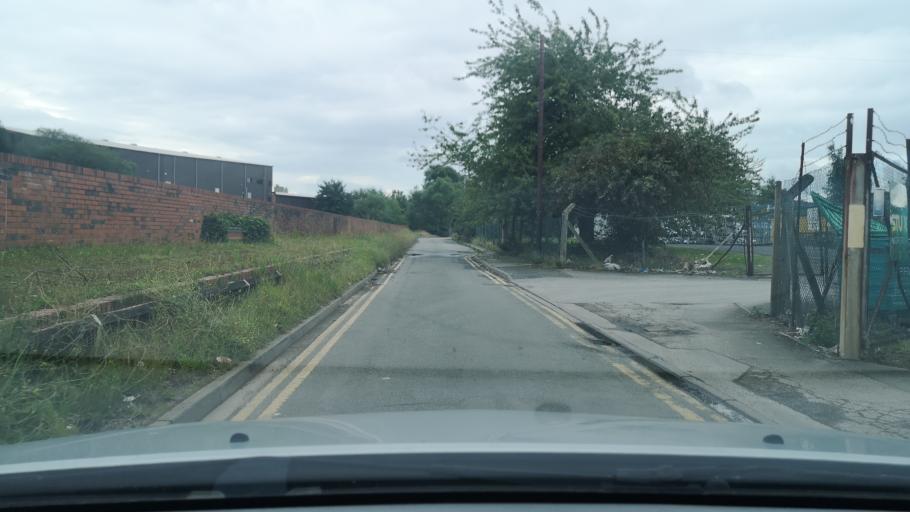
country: GB
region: England
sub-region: City and Borough of Wakefield
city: Wakefield
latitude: 53.6714
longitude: -1.4922
